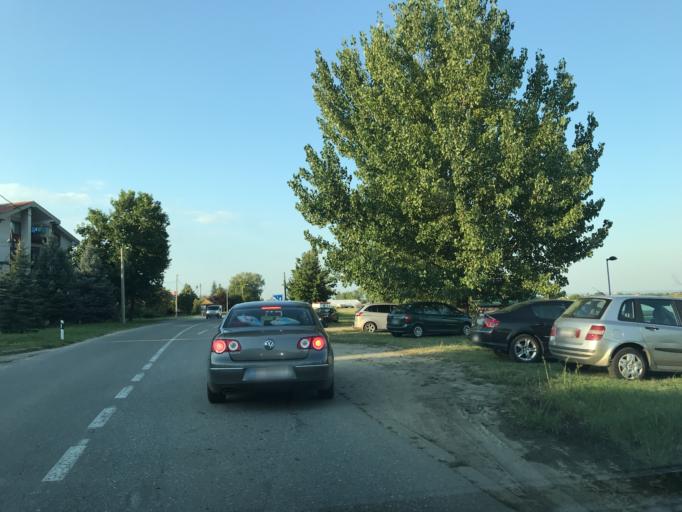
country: RO
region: Mehedinti
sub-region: Comuna Gogosu
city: Ostrovu Mare
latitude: 44.4815
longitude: 22.4541
